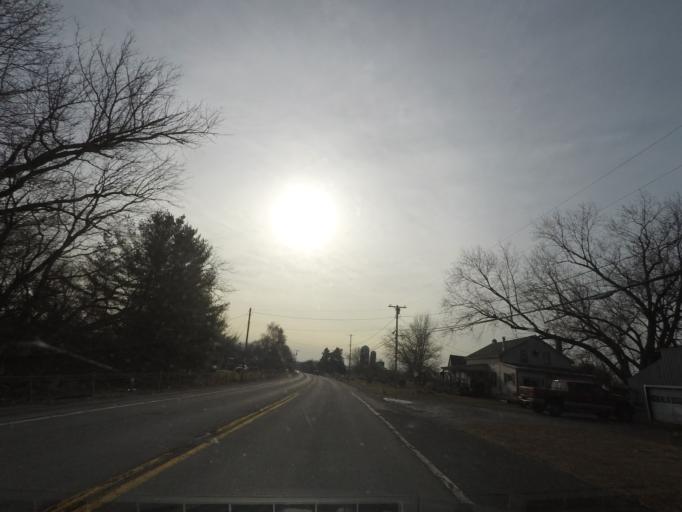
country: US
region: New York
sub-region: Saratoga County
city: Stillwater
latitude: 42.9710
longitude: -73.6335
